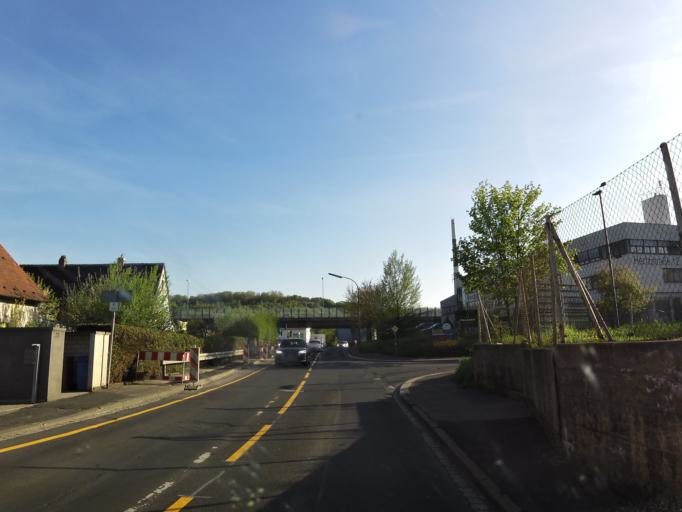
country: DE
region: Bavaria
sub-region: Regierungsbezirk Unterfranken
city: Wuerzburg
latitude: 49.8004
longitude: 9.9778
